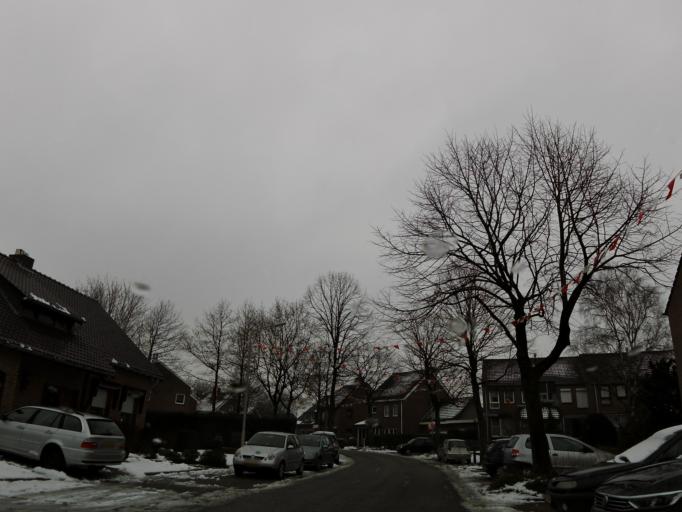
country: NL
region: Limburg
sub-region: Gemeente Kerkrade
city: Kerkrade
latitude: 50.8858
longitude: 6.0575
